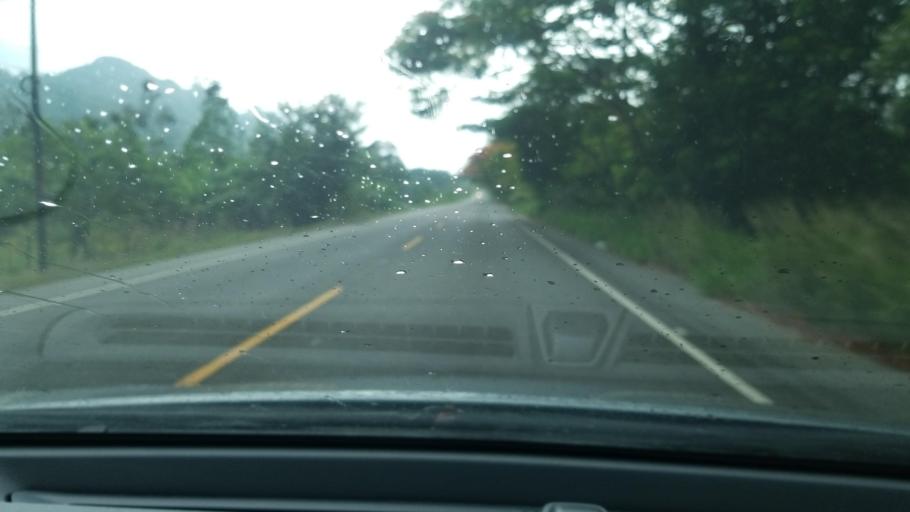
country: HN
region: Cortes
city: Rio Chiquito
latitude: 15.6217
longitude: -88.2657
